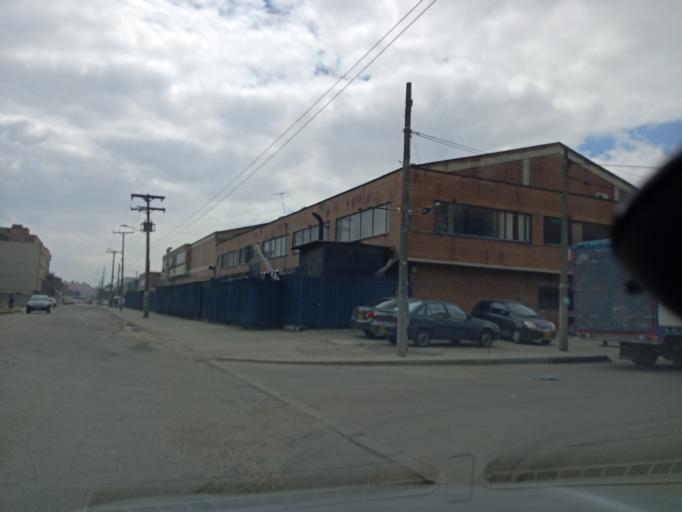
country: CO
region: Bogota D.C.
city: Bogota
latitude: 4.6508
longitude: -74.1183
